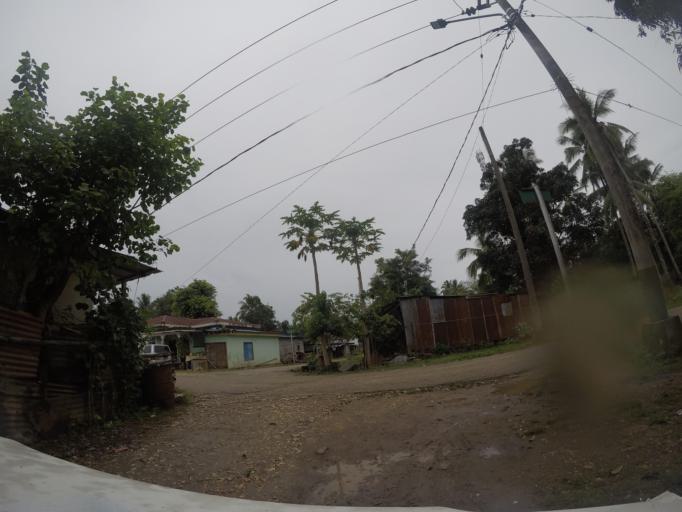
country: TL
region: Lautem
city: Lospalos
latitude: -8.5248
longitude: 126.9993
